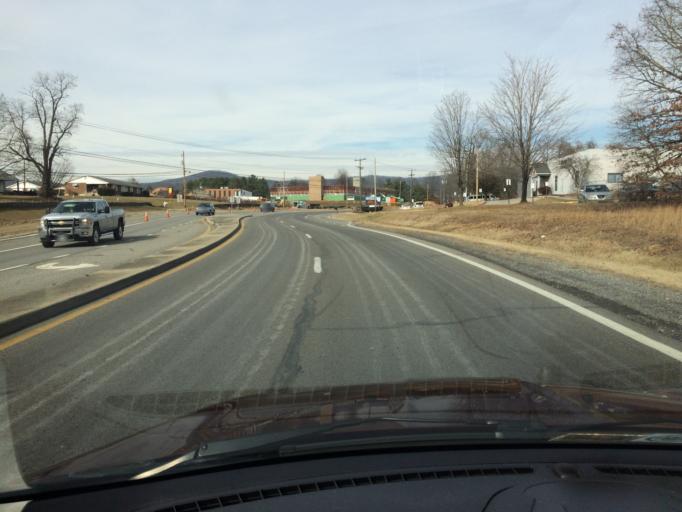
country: US
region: Virginia
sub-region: Roanoke County
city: Hollins
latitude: 37.3500
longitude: -79.9519
